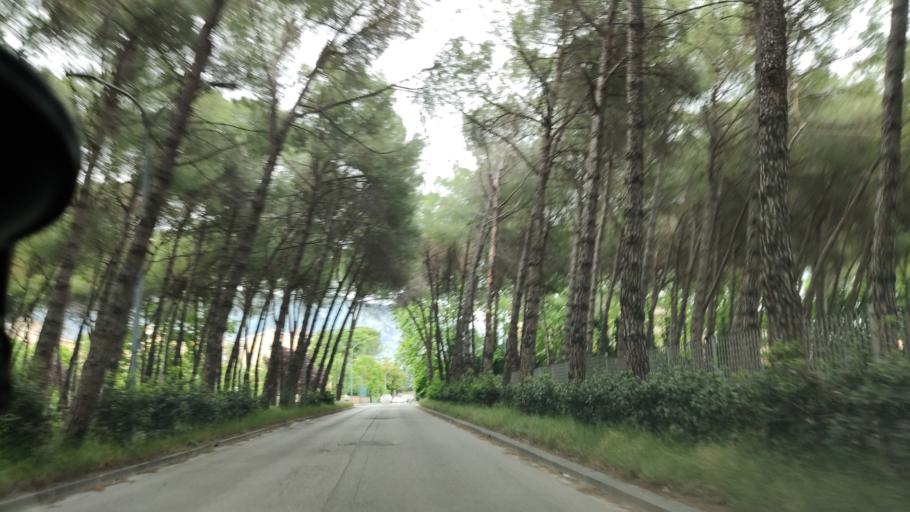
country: IT
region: Umbria
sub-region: Provincia di Terni
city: Terni
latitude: 42.5617
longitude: 12.6580
